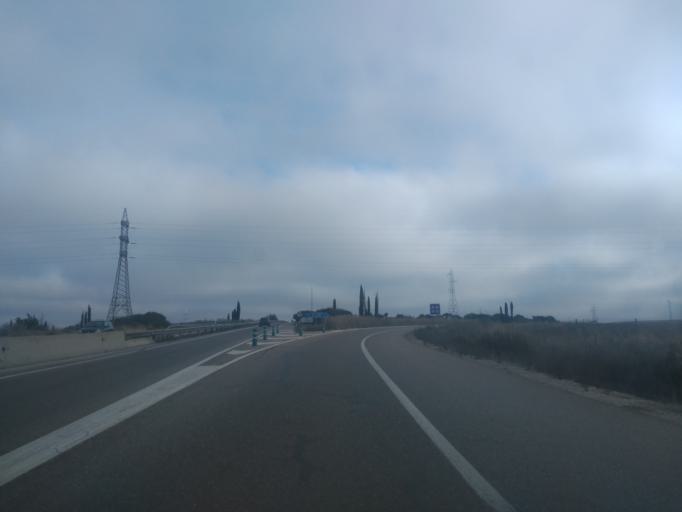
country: ES
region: Castille and Leon
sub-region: Provincia de Salamanca
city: Villares de la Reina
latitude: 40.9984
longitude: -5.6299
